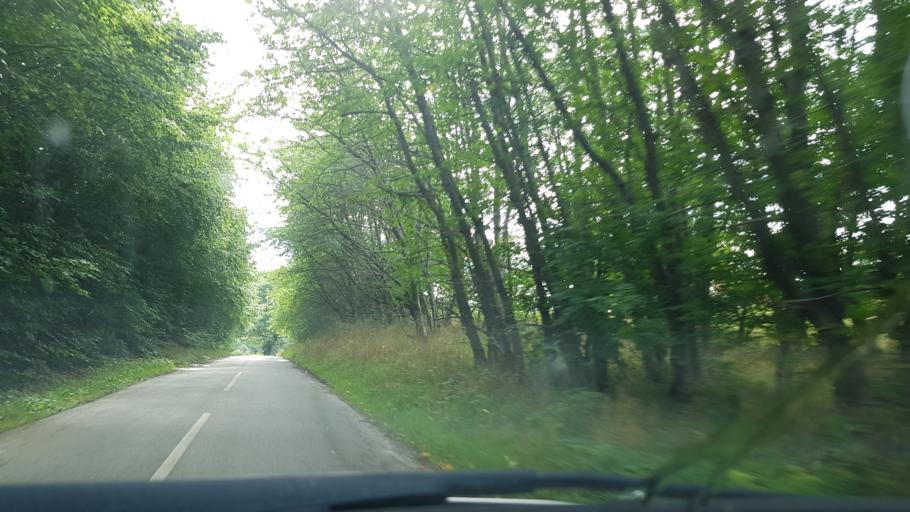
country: DK
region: Capital Region
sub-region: Fredensborg Kommune
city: Niva
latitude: 55.9759
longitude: 12.4728
